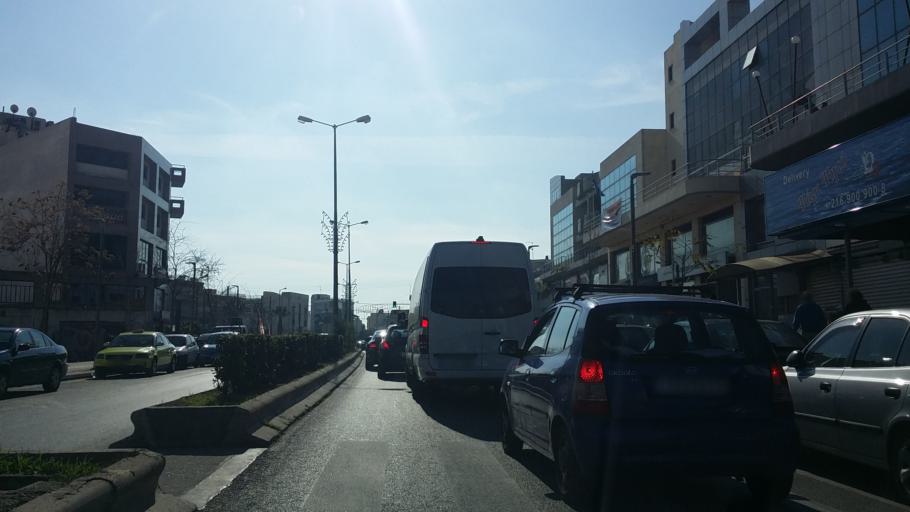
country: GR
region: Attica
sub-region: Nomarchia Athinas
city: Ilion
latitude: 38.0311
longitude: 23.7010
